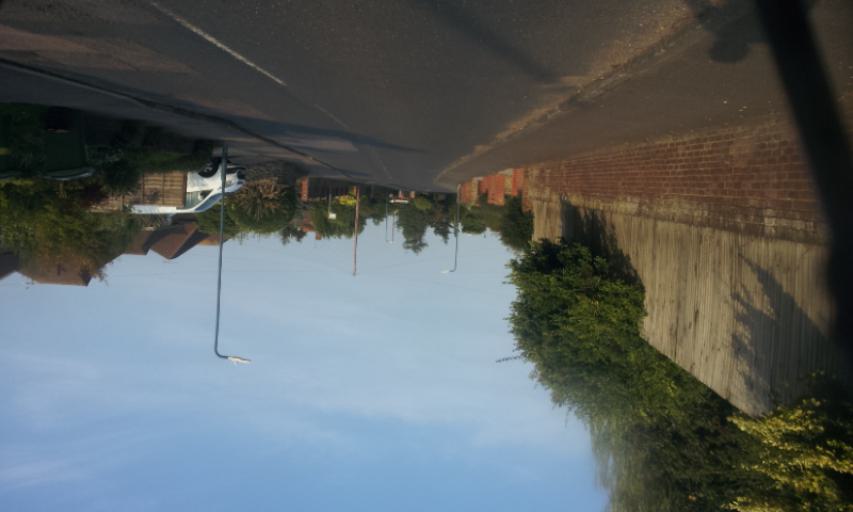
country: GB
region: England
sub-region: Kent
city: Aylesford
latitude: 51.2680
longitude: 0.4754
